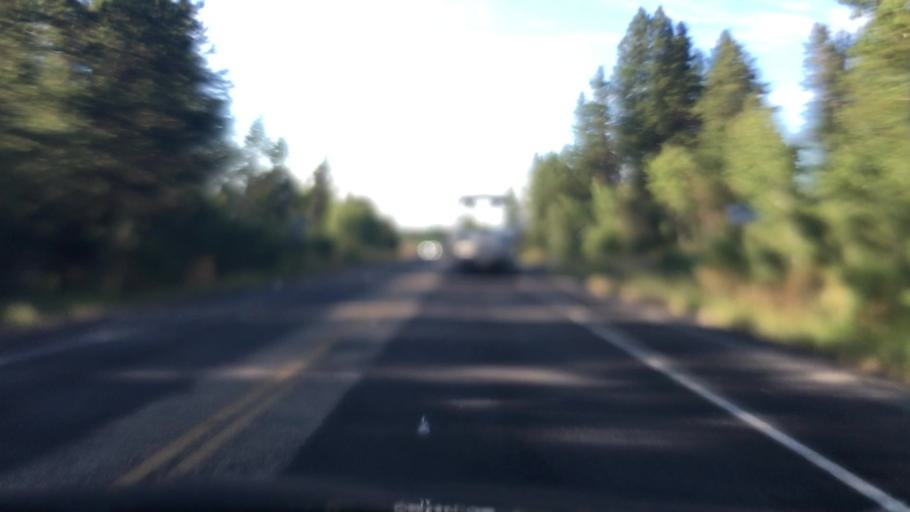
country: US
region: Idaho
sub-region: Valley County
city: Cascade
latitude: 44.6906
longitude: -116.0512
